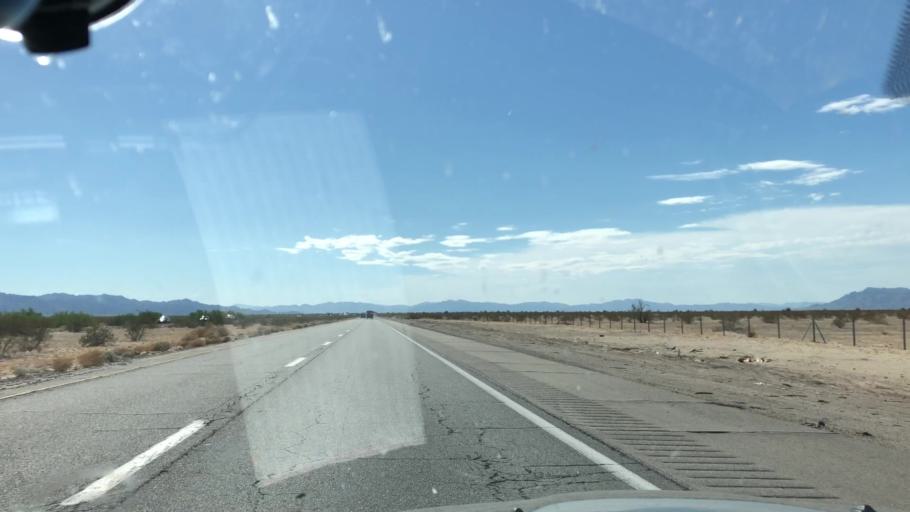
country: US
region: California
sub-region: Riverside County
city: Mesa Verde
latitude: 33.6465
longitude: -115.1213
